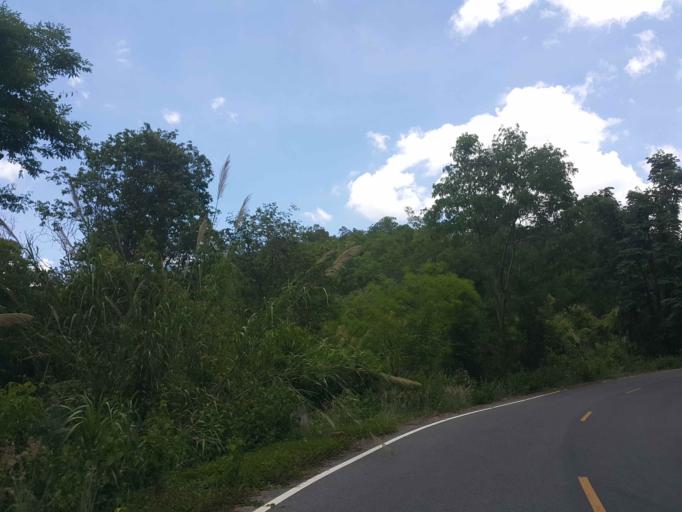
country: TH
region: Nan
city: Wiang Sa
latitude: 18.5340
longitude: 100.5505
